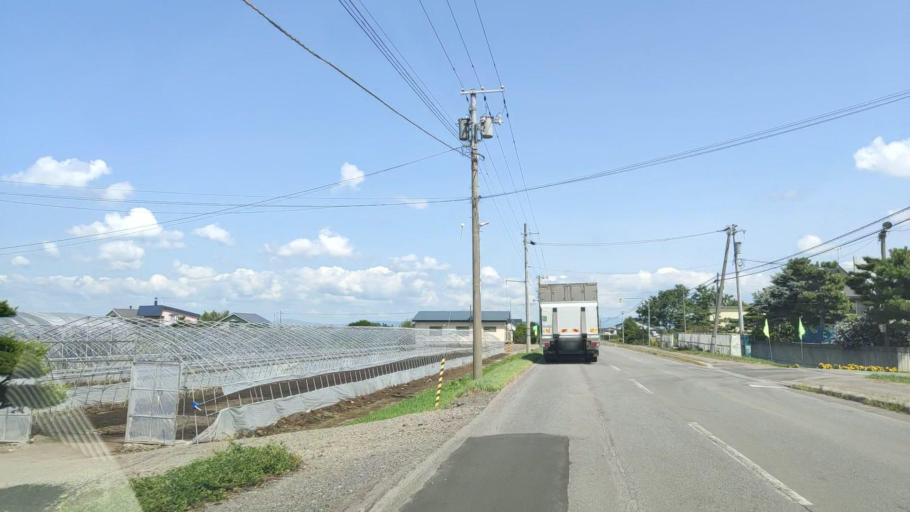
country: JP
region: Hokkaido
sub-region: Asahikawa-shi
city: Asahikawa
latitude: 43.7172
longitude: 142.4575
